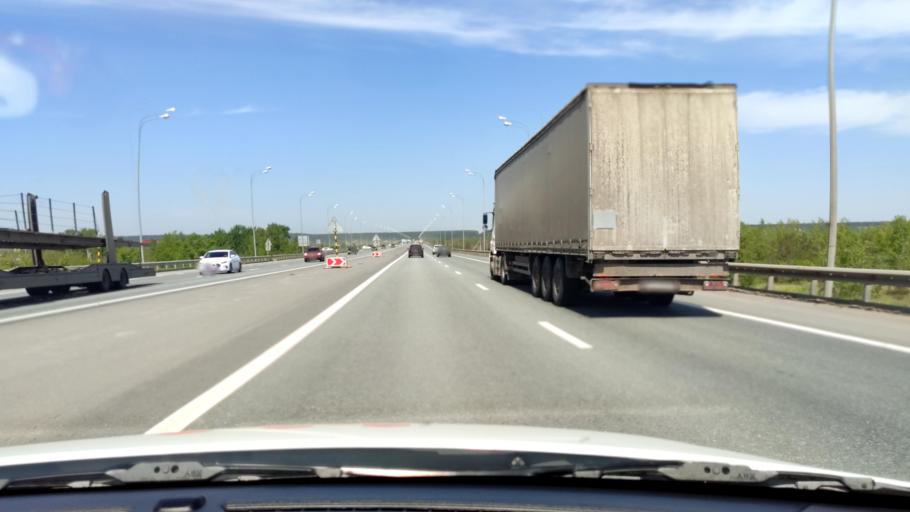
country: RU
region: Tatarstan
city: Osinovo
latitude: 55.7928
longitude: 48.8410
